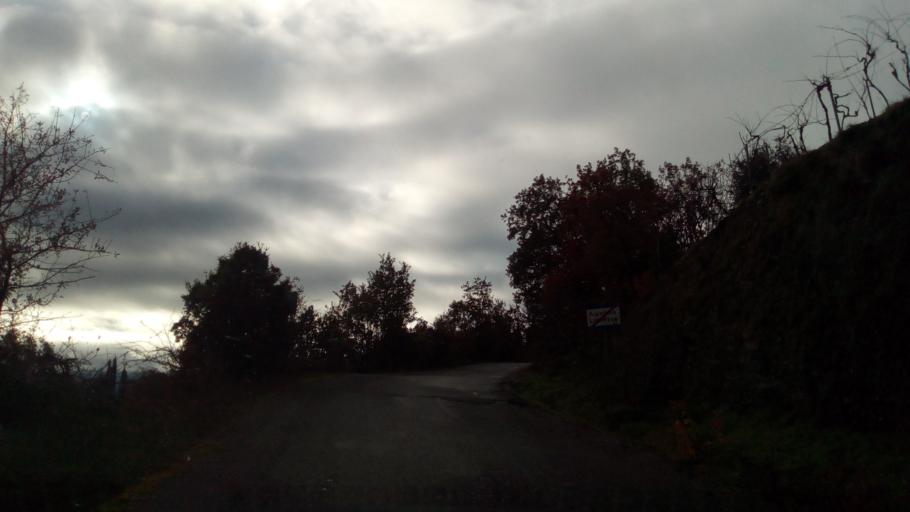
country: GR
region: West Greece
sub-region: Nomos Aitolias kai Akarnanias
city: Nafpaktos
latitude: 38.5256
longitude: 21.9778
